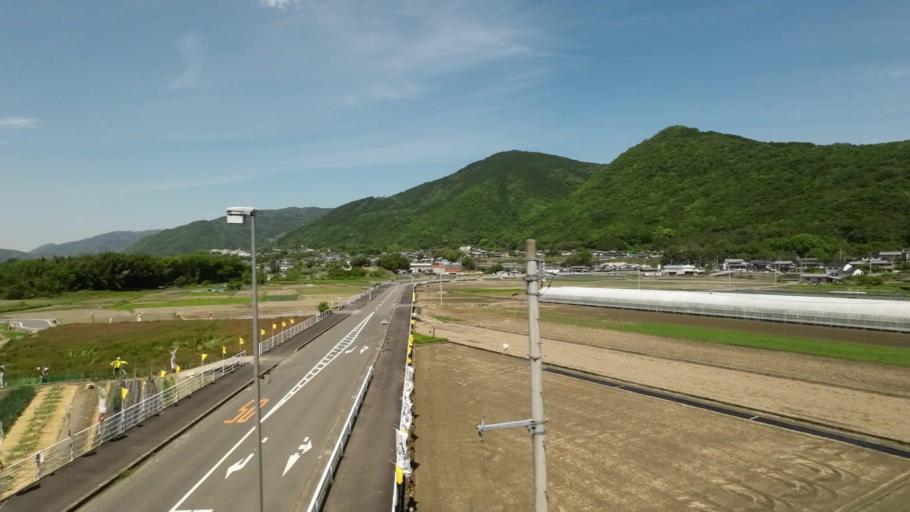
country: JP
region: Tokushima
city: Ikedacho
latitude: 34.0382
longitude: 133.8653
